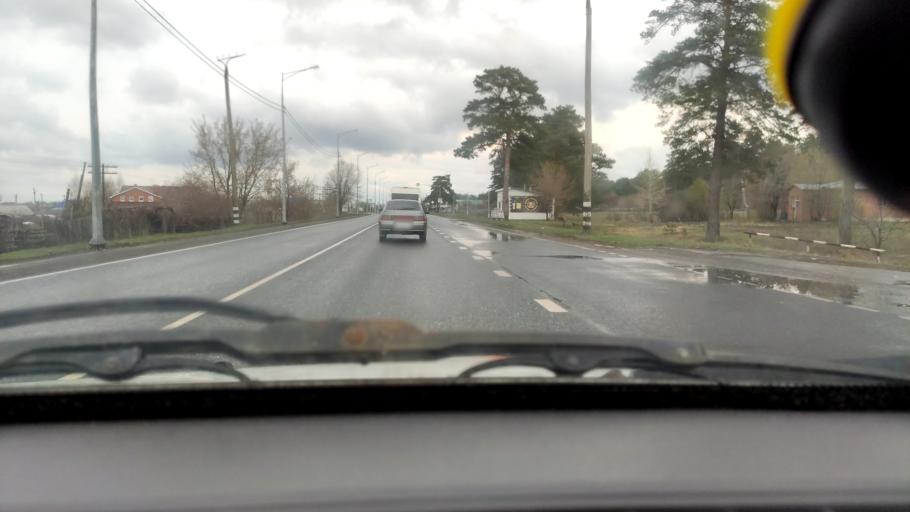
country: RU
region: Samara
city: Povolzhskiy
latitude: 53.5848
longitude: 49.5706
